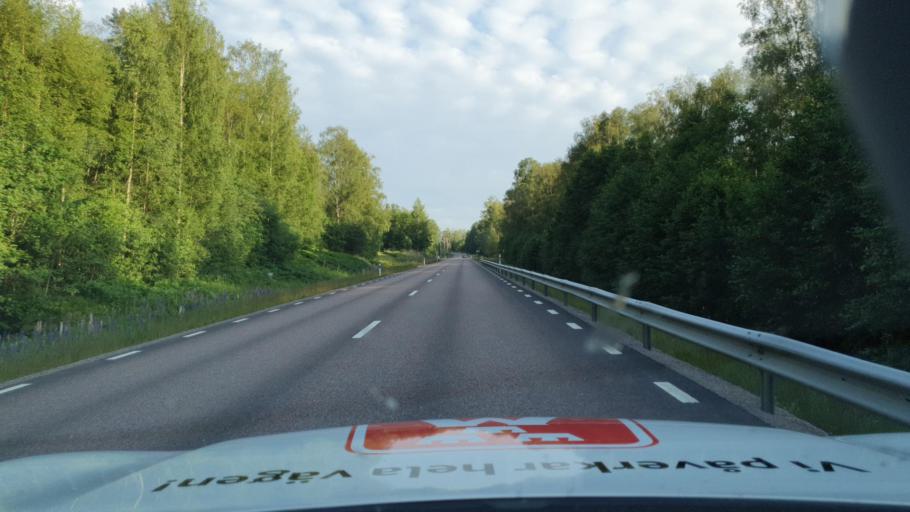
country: SE
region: Vaermland
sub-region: Hagfors Kommun
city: Hagfors
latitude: 59.9697
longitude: 13.6577
